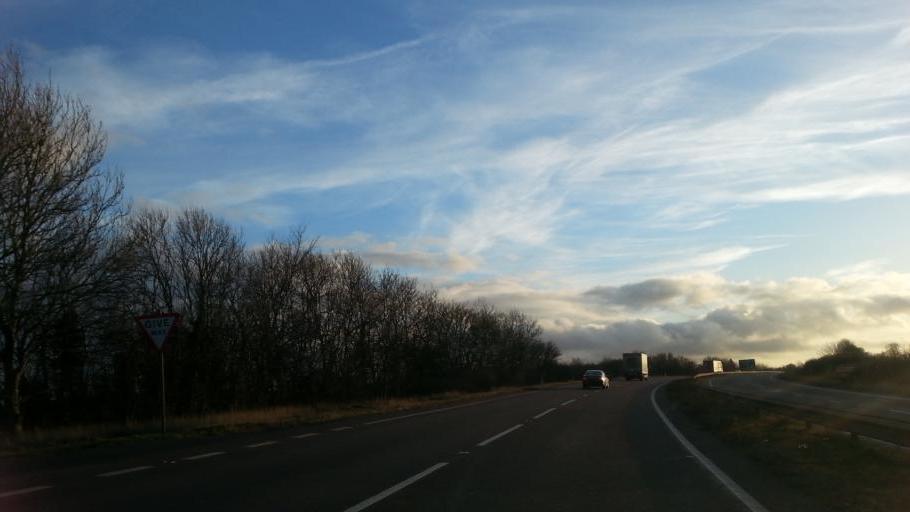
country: GB
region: England
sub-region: Northamptonshire
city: Brackley
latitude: 52.0031
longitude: -1.1581
